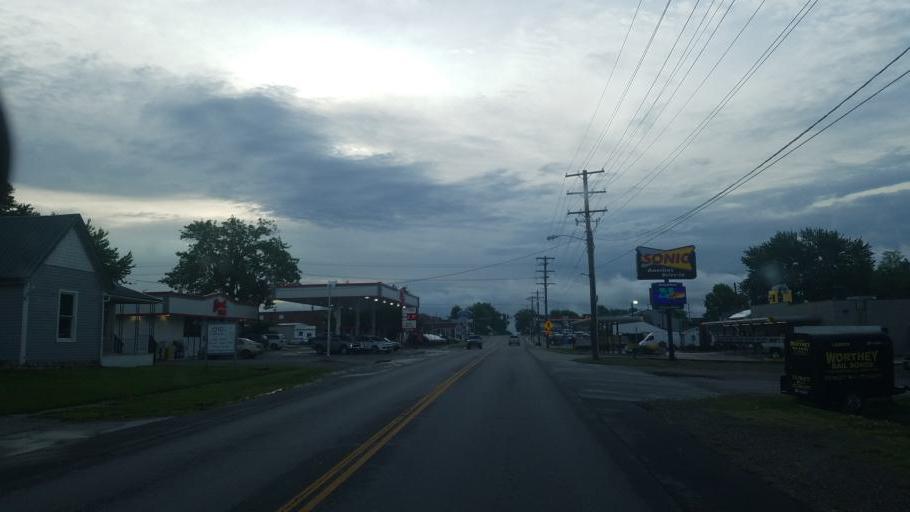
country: US
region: Missouri
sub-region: Moniteau County
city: California
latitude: 38.6276
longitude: -92.5692
